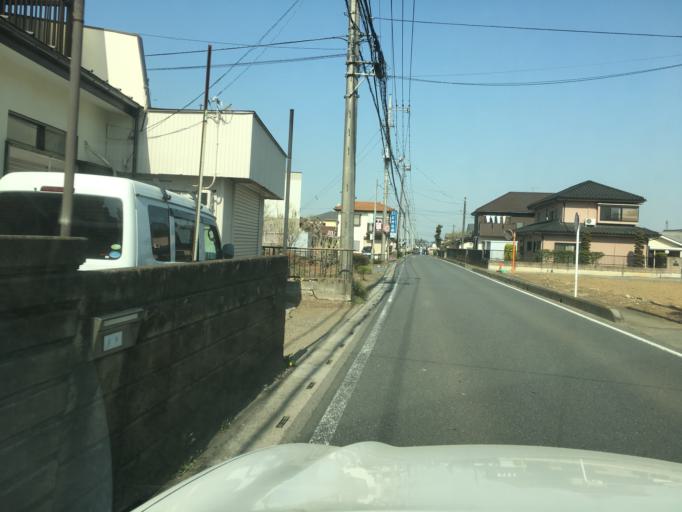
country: JP
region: Saitama
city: Sayama
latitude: 35.8525
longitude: 139.4544
